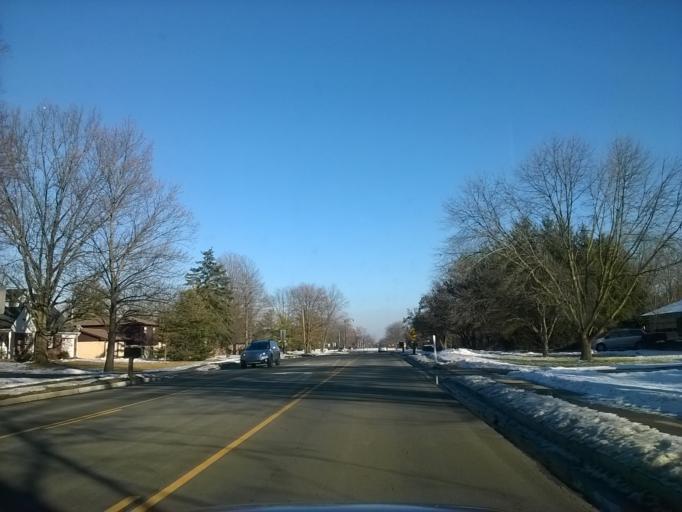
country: US
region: Indiana
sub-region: Hamilton County
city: Carmel
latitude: 39.9784
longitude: -86.1159
